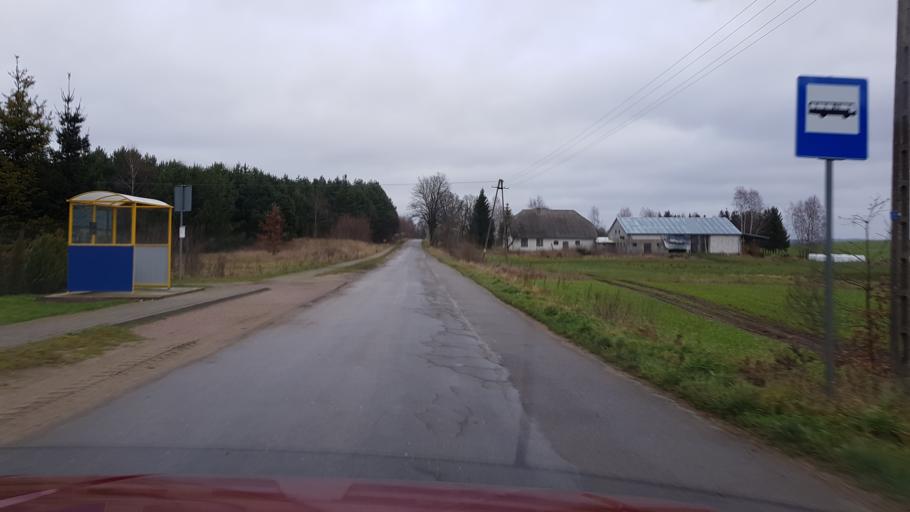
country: PL
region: Pomeranian Voivodeship
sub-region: Powiat bytowski
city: Tuchomie
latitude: 54.1539
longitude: 17.3276
